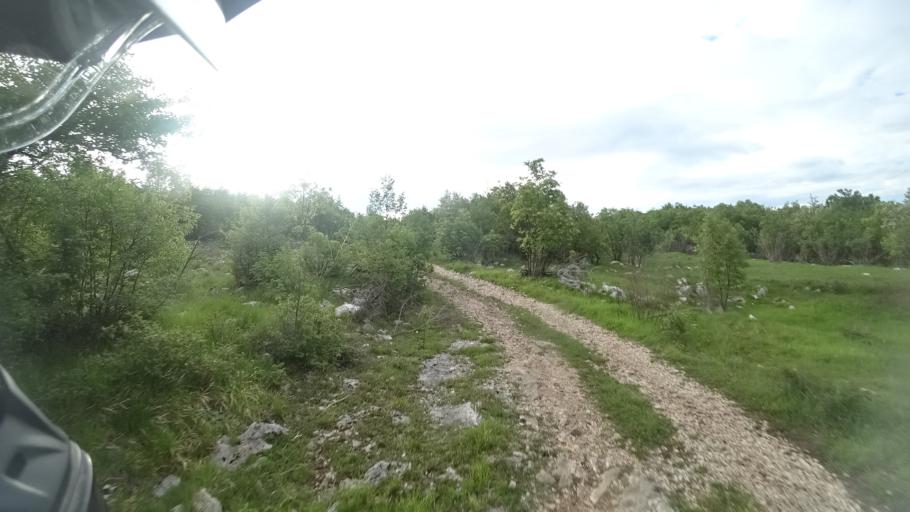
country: HR
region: Sibensko-Kniniska
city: Drnis
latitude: 43.8703
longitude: 16.3825
